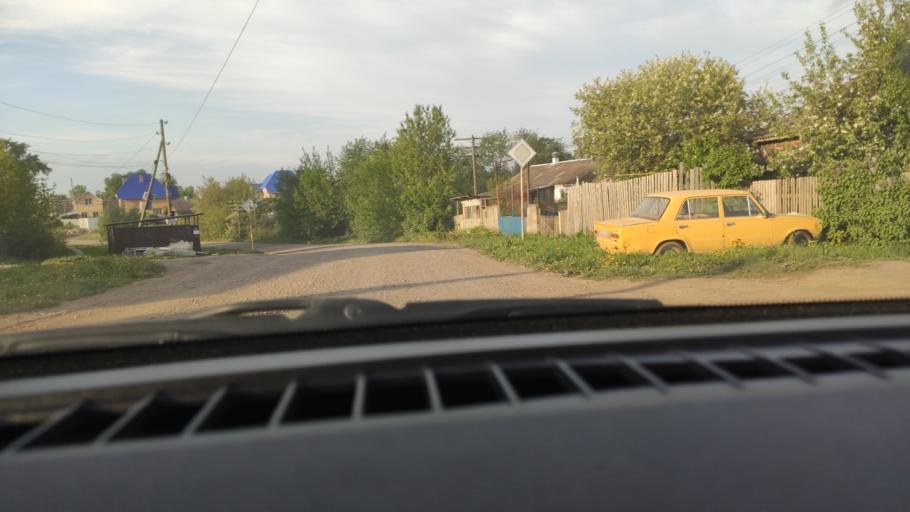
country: RU
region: Perm
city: Kultayevo
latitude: 57.9297
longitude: 56.0156
